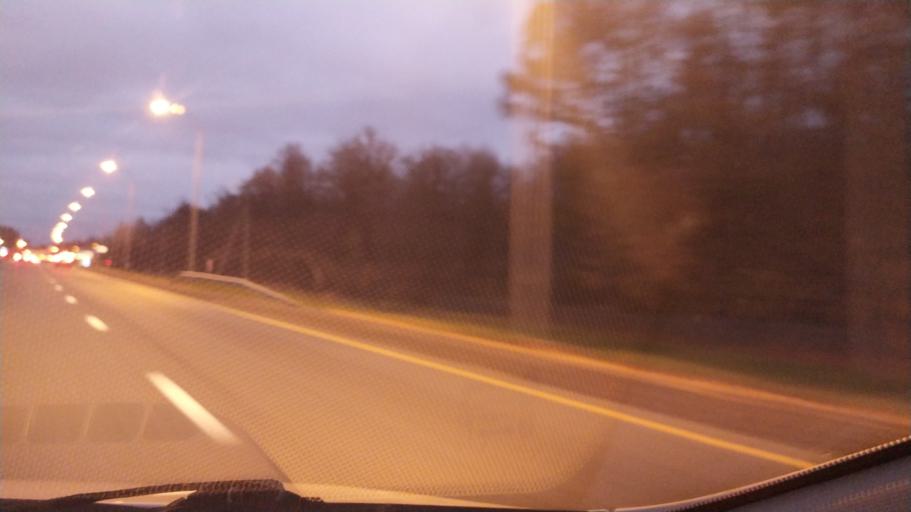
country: RU
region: Chuvashia
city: Kugesi
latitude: 56.0394
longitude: 47.2939
